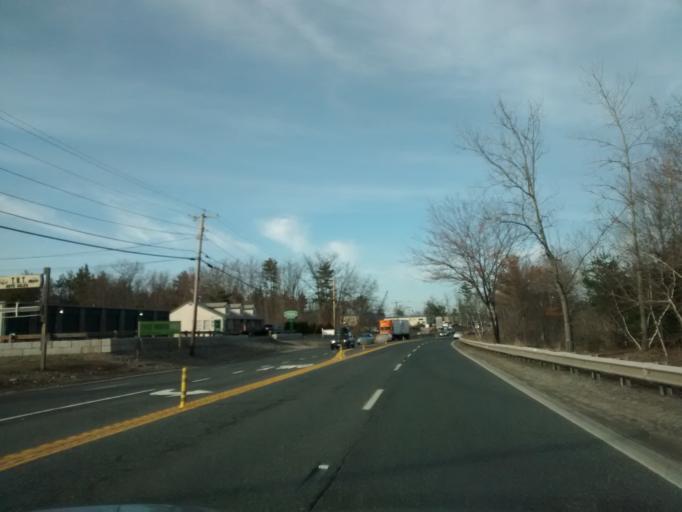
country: US
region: Massachusetts
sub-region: Worcester County
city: Oxford
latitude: 42.1626
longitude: -71.8992
